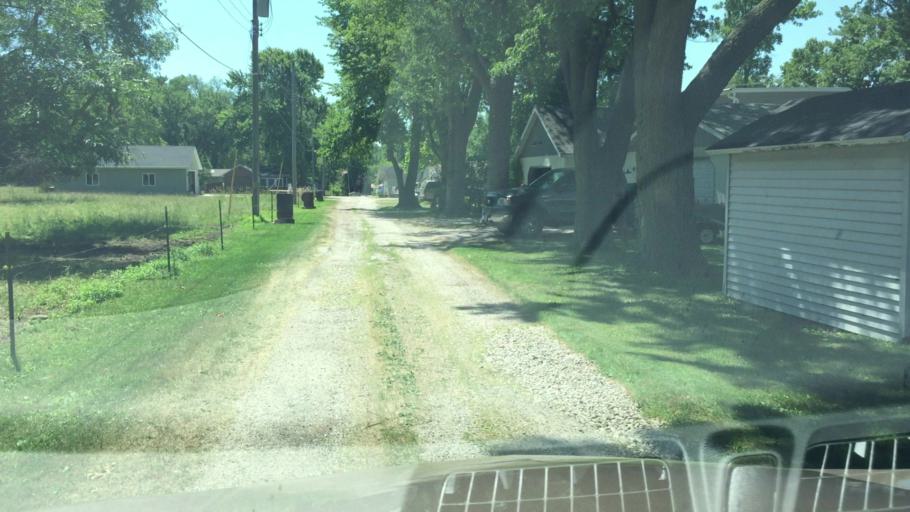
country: US
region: Wisconsin
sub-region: Fond du Lac County
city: Saint Peter
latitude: 43.9614
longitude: -88.3191
